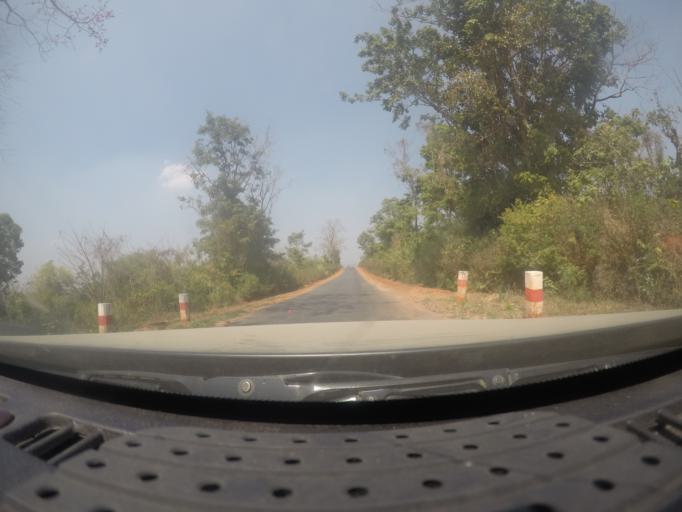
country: MM
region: Shan
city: Taunggyi
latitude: 21.0097
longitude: 96.5272
